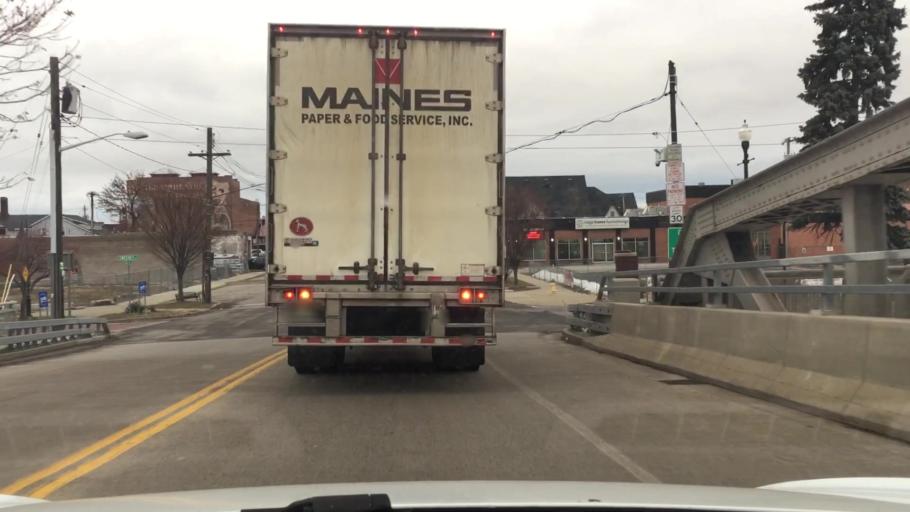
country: US
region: New York
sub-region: Erie County
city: Tonawanda
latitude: 43.0218
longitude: -78.8756
